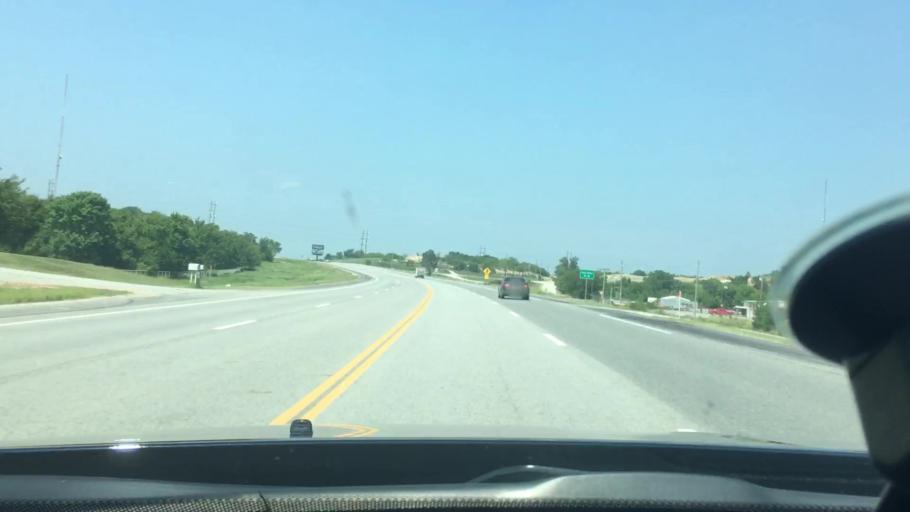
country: US
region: Oklahoma
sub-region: Atoka County
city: Atoka
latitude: 34.3703
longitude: -96.1056
